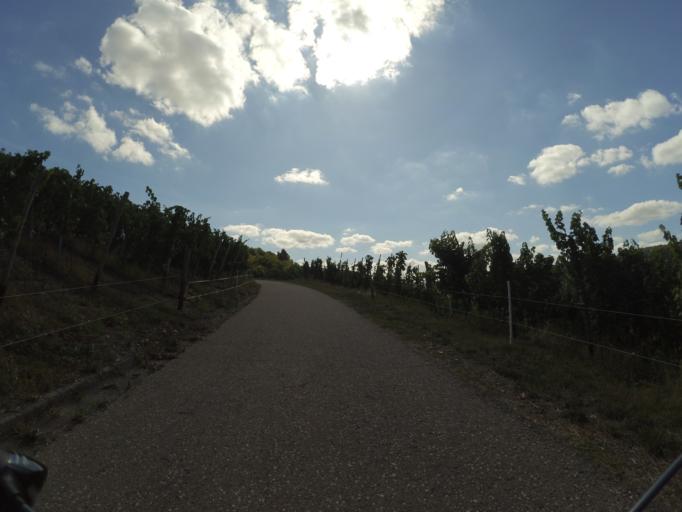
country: DE
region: Rheinland-Pfalz
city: Kasel
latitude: 49.7579
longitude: 6.7373
